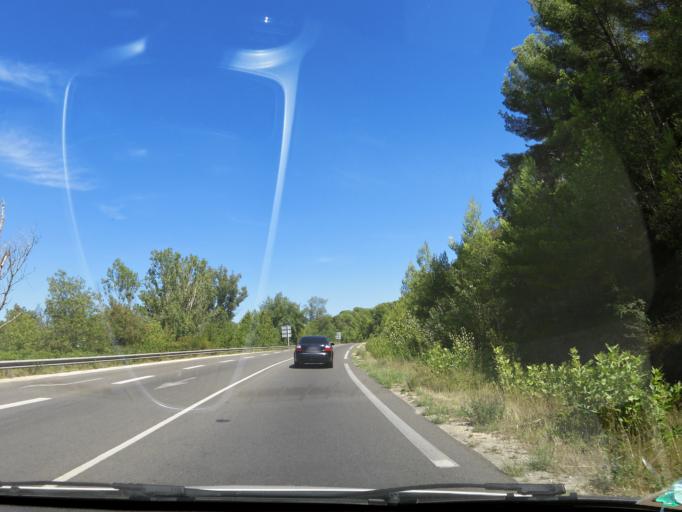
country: FR
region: Languedoc-Roussillon
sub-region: Departement de l'Herault
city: Castelnau-le-Lez
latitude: 43.6443
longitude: 3.8995
